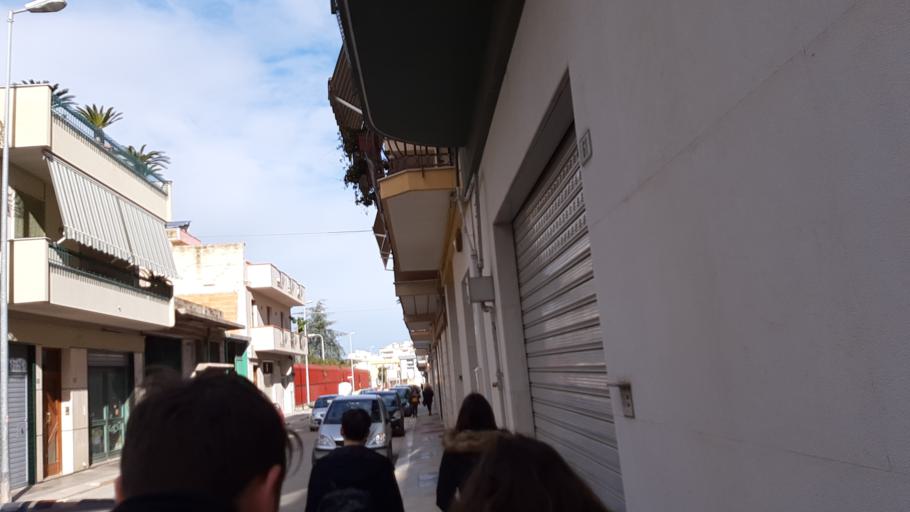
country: IT
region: Apulia
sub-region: Provincia di Barletta - Andria - Trani
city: Andria
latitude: 41.2342
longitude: 16.2929
